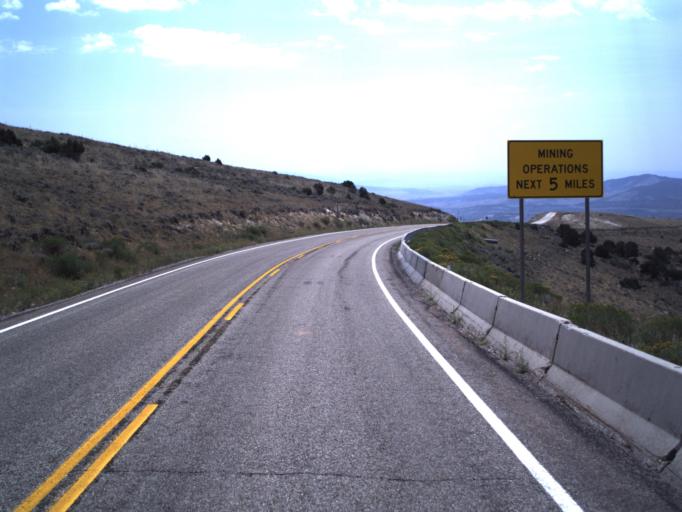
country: US
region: Utah
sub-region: Uintah County
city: Maeser
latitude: 40.6530
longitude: -109.4905
